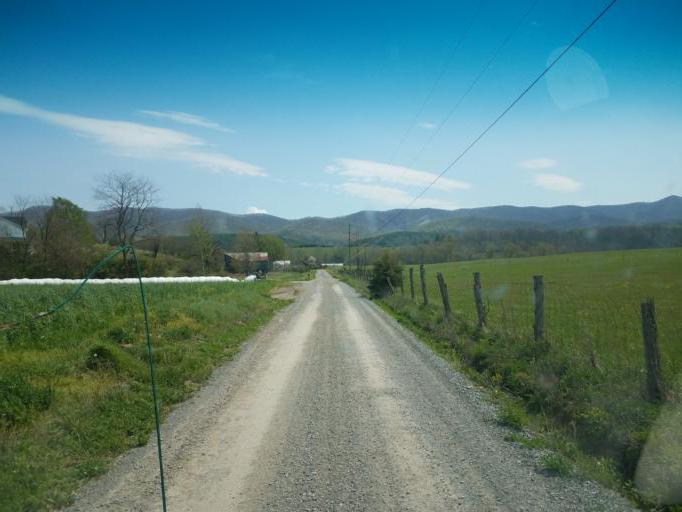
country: US
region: Virginia
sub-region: Smyth County
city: Marion
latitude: 36.7776
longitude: -81.4546
